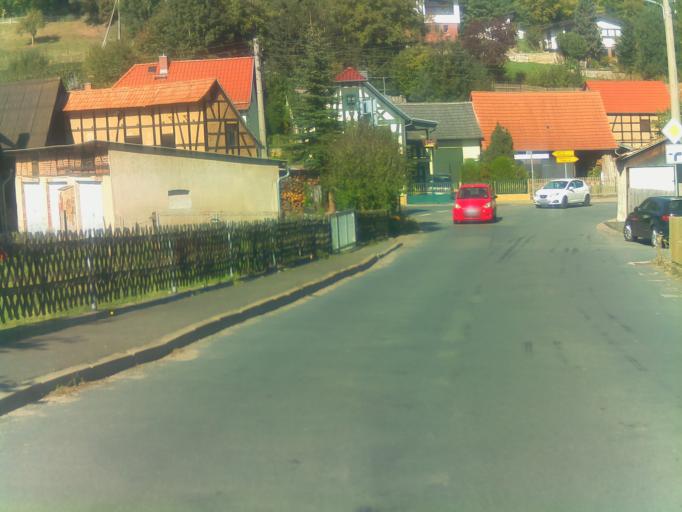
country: DE
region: Thuringia
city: Geisenhain
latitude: 50.8341
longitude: 11.7148
